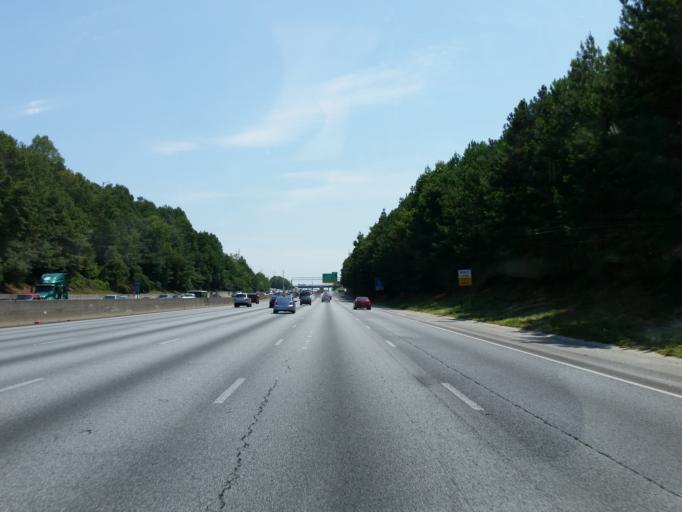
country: US
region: Georgia
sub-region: DeKalb County
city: Dunwoody
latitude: 33.9201
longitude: -84.3256
